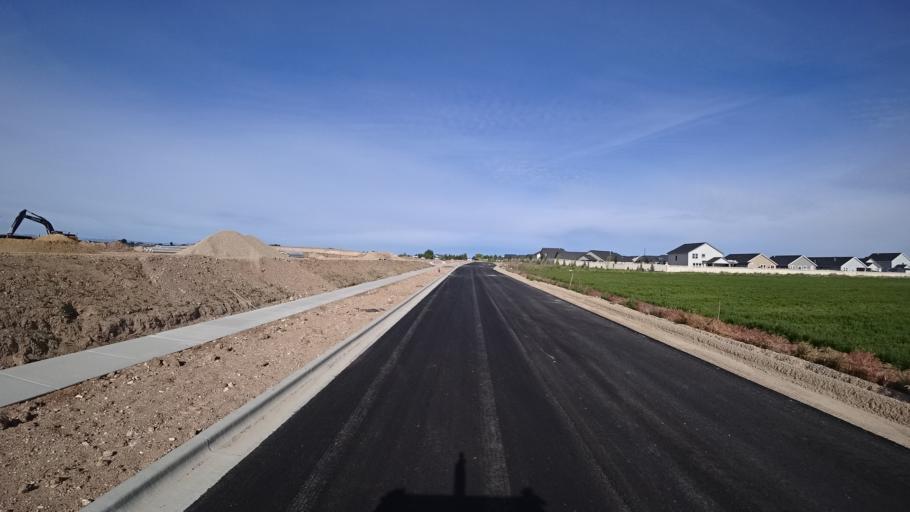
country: US
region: Idaho
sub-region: Ada County
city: Kuna
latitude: 43.5100
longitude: -116.3980
